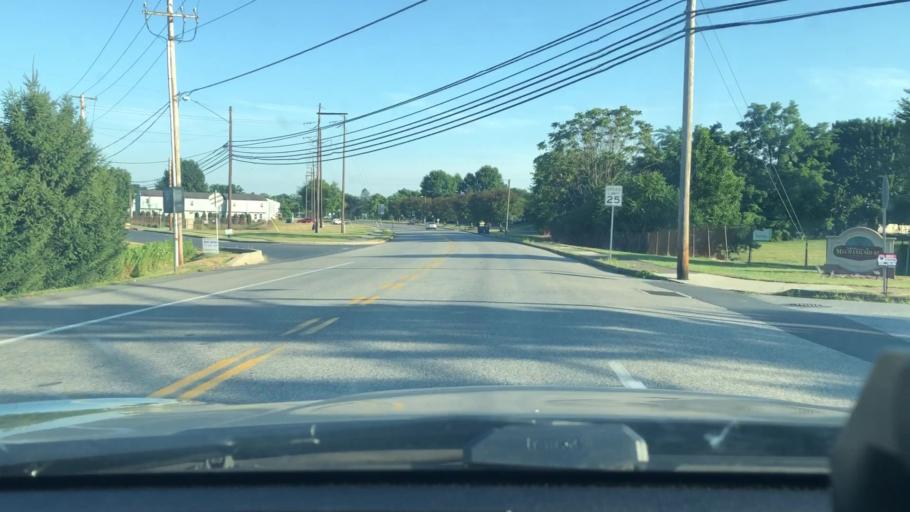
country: US
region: Pennsylvania
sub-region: Cumberland County
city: Mechanicsburg
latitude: 40.2239
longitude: -77.0077
